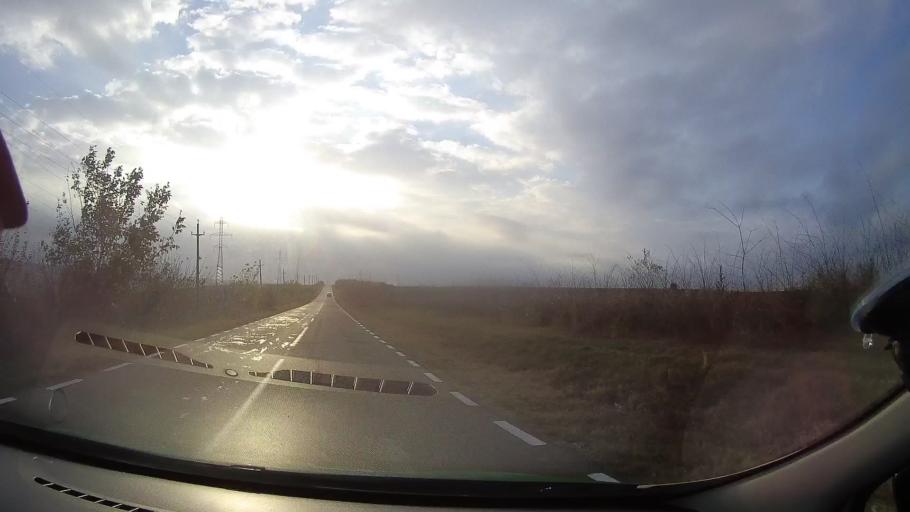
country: RO
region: Constanta
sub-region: Comuna Pestera
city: Pestera
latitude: 44.2112
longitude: 28.1792
